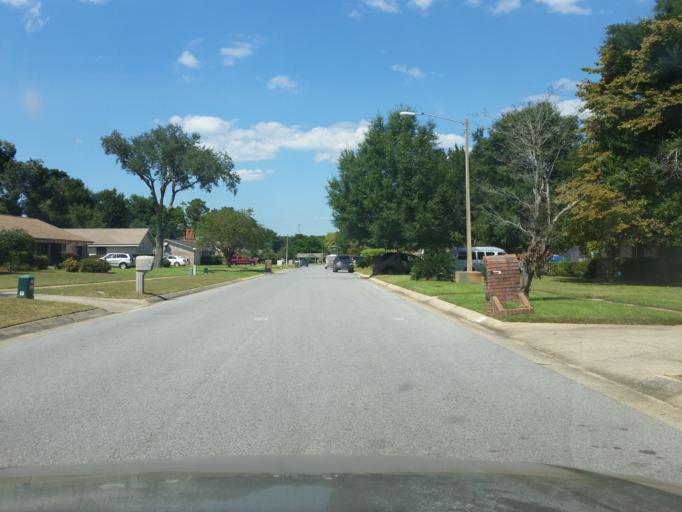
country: US
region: Florida
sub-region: Escambia County
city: Ferry Pass
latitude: 30.5107
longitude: -87.1875
